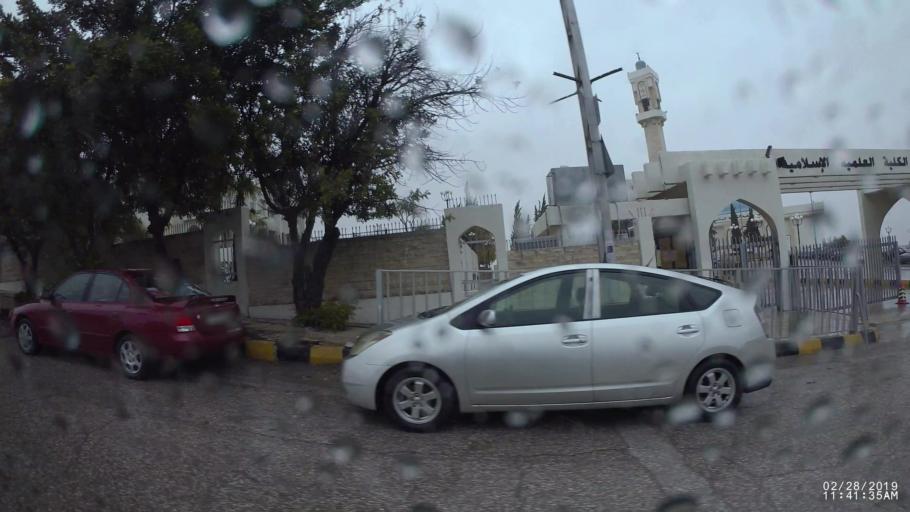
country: JO
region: Amman
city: Al Jubayhah
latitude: 32.0161
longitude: 35.8914
